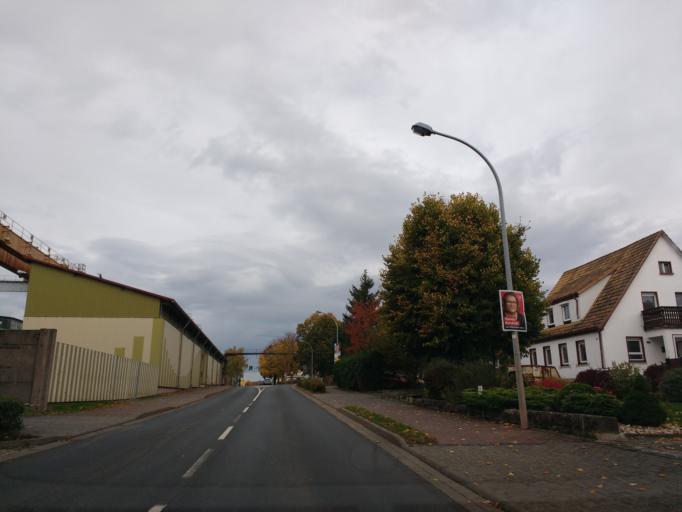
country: DE
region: Thuringia
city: Niederorschel
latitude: 51.3794
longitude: 10.4174
